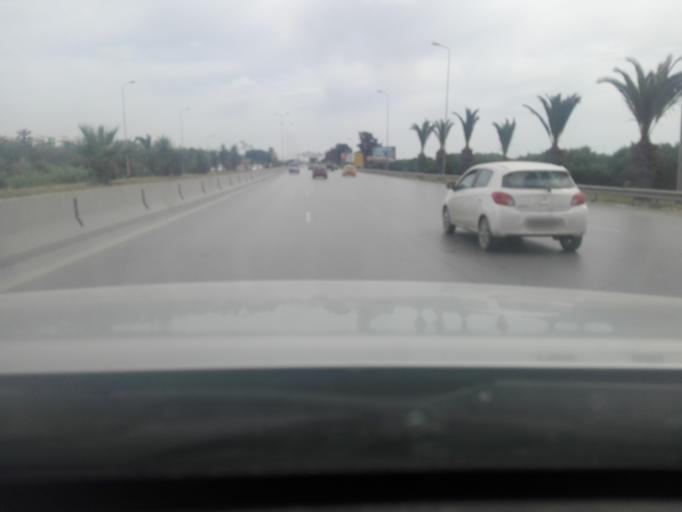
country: TN
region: Tunis
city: Tunis
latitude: 36.8175
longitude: 10.1929
